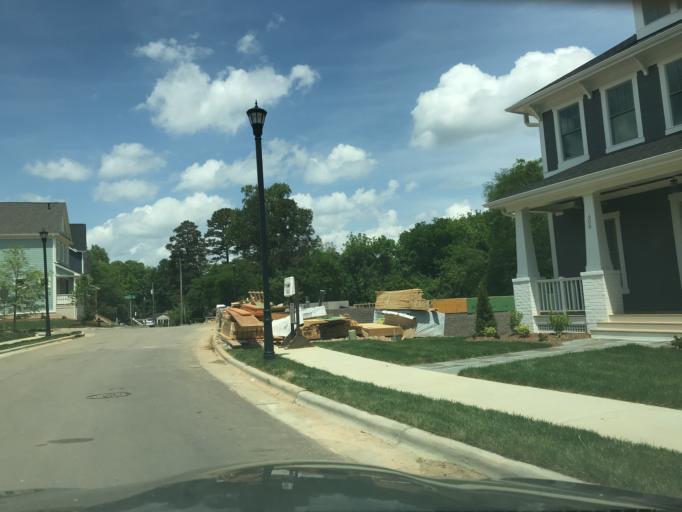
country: US
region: North Carolina
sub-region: Wake County
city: Raleigh
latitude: 35.7916
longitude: -78.6267
